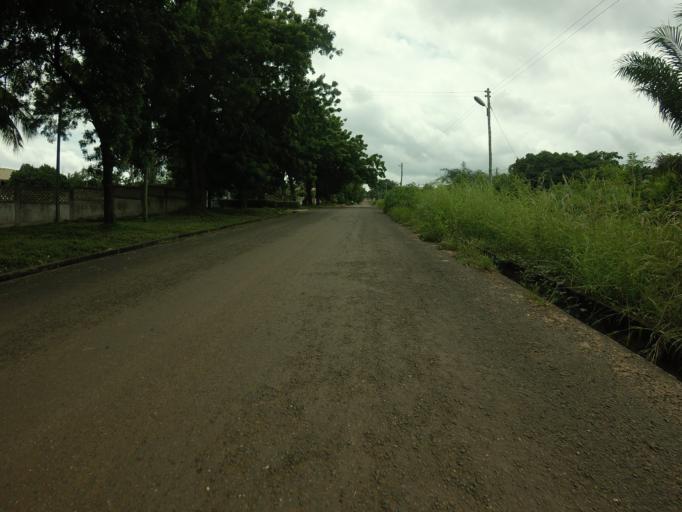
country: GH
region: Volta
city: Ho
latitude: 6.5963
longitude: 0.4592
